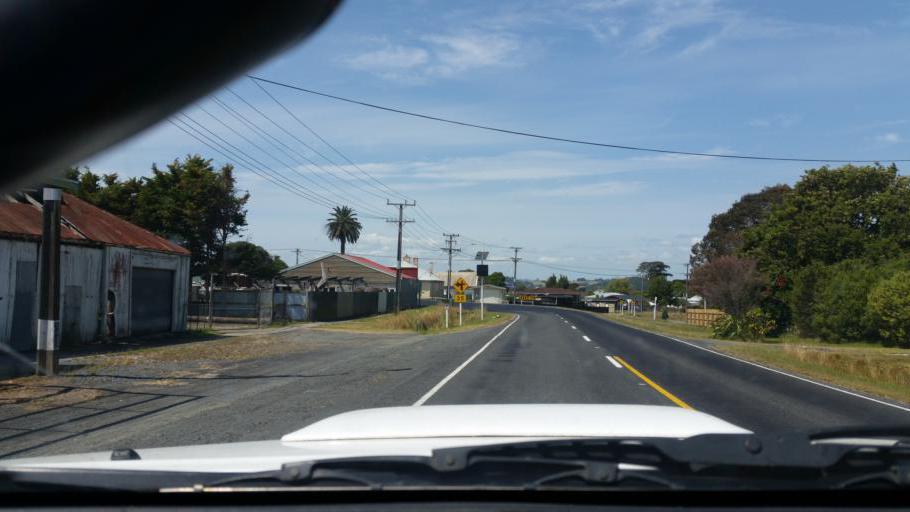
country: NZ
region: Northland
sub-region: Kaipara District
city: Dargaville
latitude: -36.0315
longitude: 173.9225
